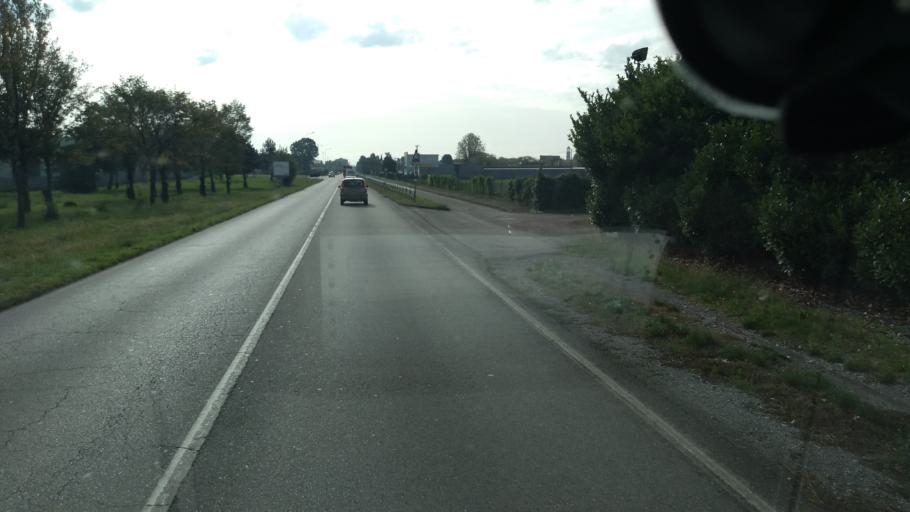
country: IT
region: Lombardy
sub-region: Provincia di Bergamo
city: Urgnano
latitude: 45.6099
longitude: 9.6952
